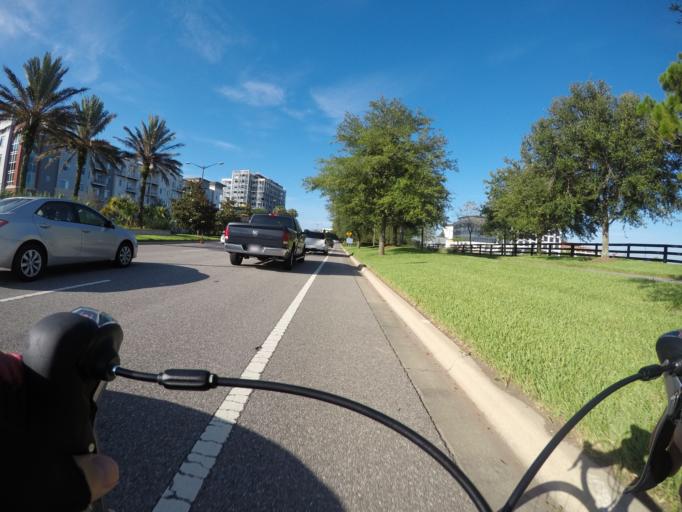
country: US
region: Florida
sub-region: Osceola County
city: Buenaventura Lakes
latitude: 28.3738
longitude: -81.2773
